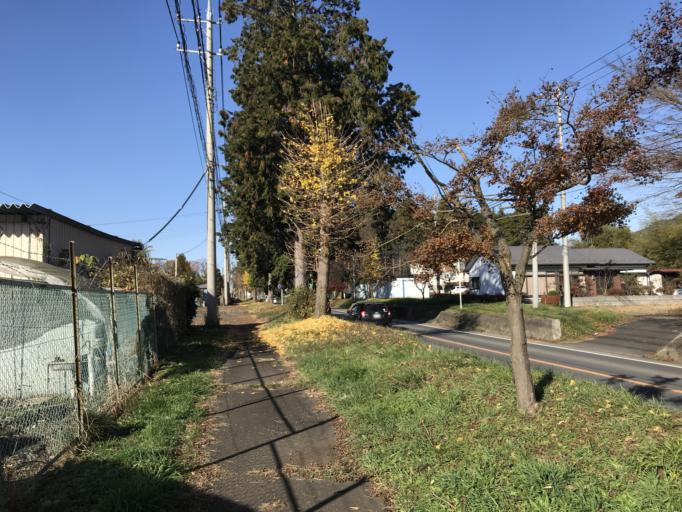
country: JP
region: Tochigi
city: Kanuma
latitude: 36.5946
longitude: 139.7454
